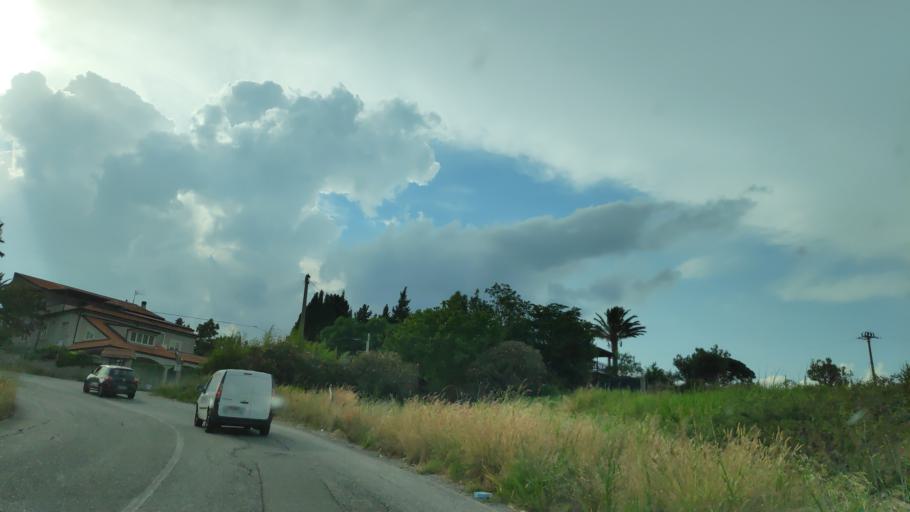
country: IT
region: Calabria
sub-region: Provincia di Catanzaro
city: Martelli-Laganosa
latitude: 38.6784
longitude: 16.5123
